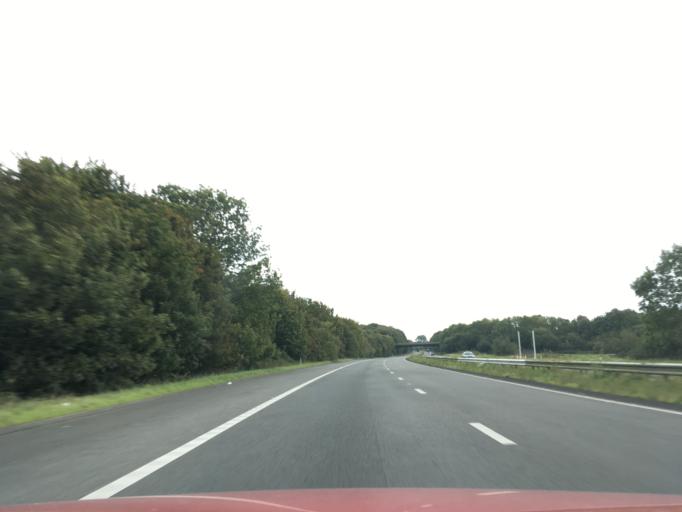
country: GB
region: Wales
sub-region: Monmouthshire
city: Chepstow
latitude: 51.6178
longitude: -2.7153
